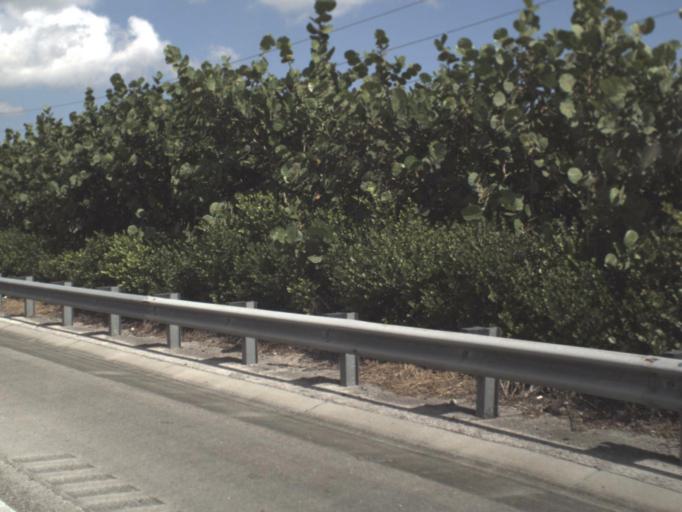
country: US
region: Florida
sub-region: Saint Lucie County
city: River Park
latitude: 27.3457
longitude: -80.3742
